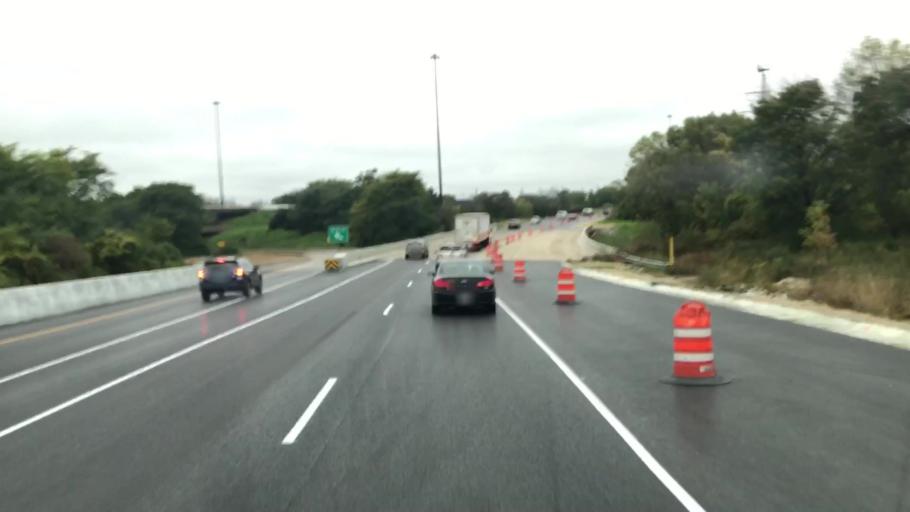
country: US
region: Wisconsin
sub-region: Milwaukee County
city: Greenfield
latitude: 42.9630
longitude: -88.0344
